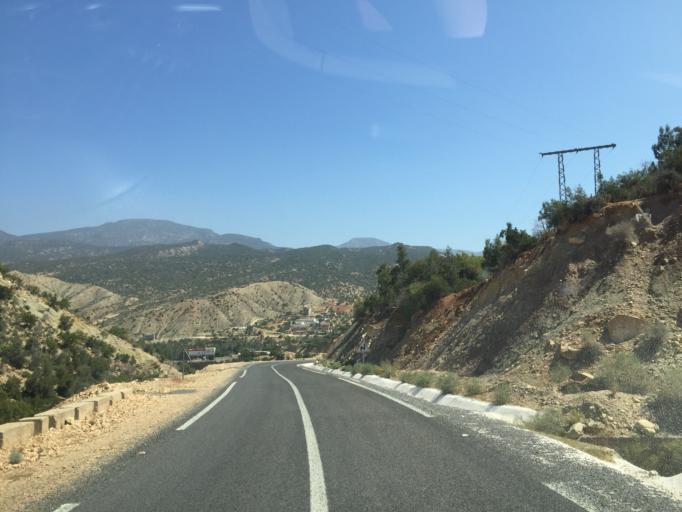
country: MA
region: Souss-Massa-Draa
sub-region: Agadir-Ida-ou-Tnan
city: Aourir
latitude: 30.5472
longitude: -9.5643
